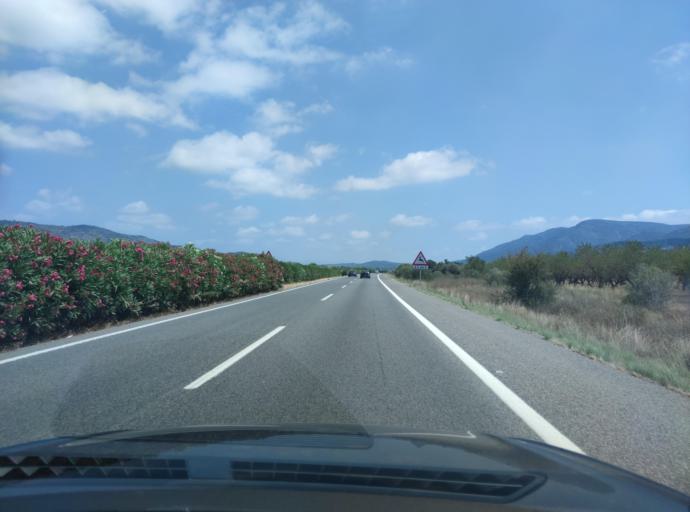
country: ES
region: Catalonia
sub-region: Provincia de Tarragona
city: Ulldecona
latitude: 40.6159
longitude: 0.4811
